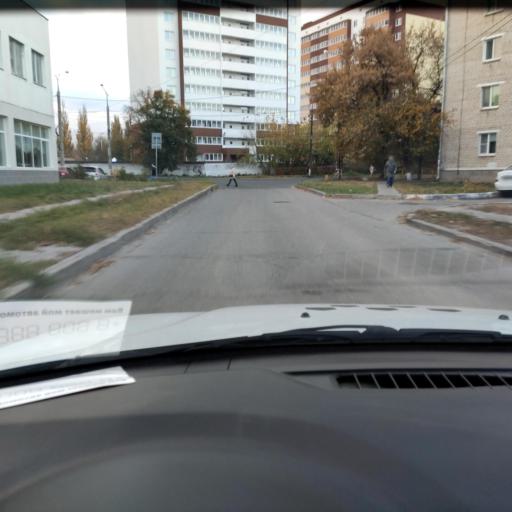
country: RU
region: Samara
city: Tol'yatti
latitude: 53.5230
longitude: 49.4179
